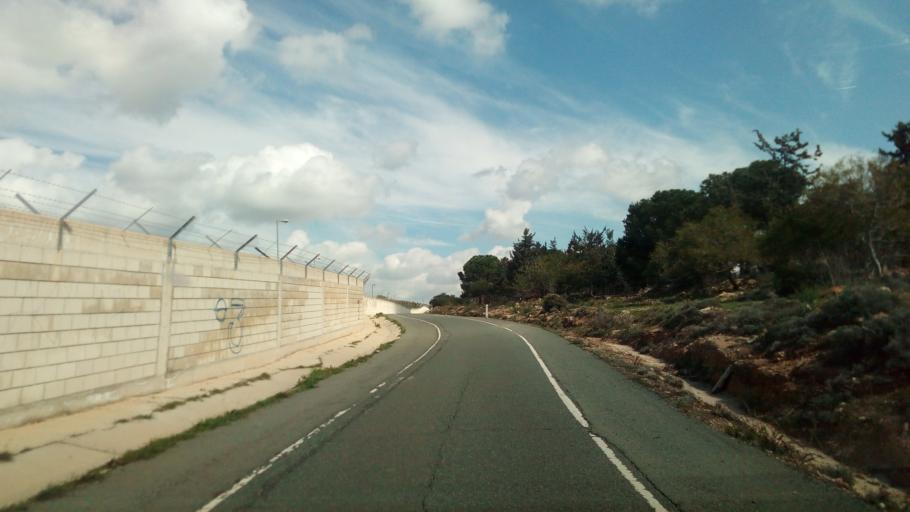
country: CY
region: Pafos
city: Mesogi
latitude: 34.7488
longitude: 32.5480
